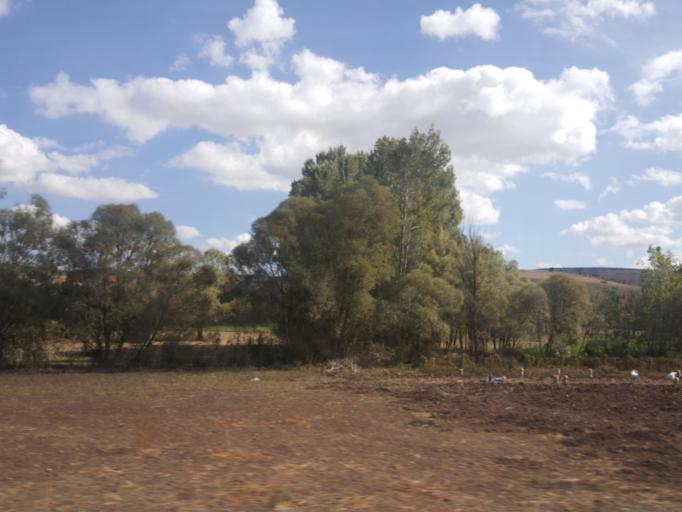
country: TR
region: Tokat
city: Camlibel
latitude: 40.1665
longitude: 36.4271
